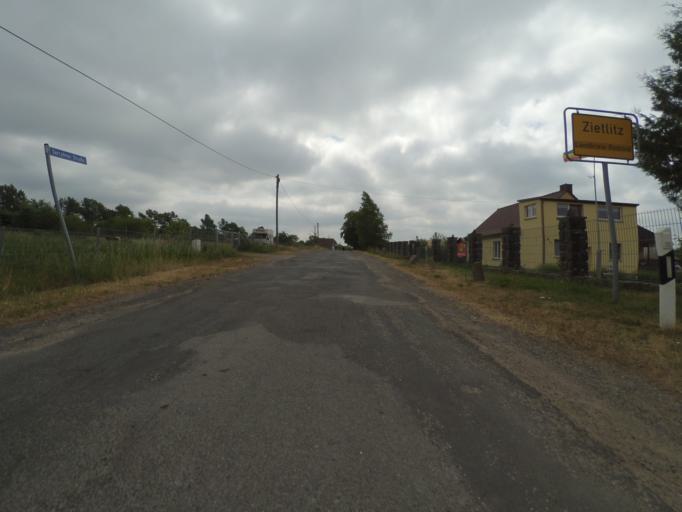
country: DE
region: Mecklenburg-Vorpommern
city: Krakow am See
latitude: 53.6349
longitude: 12.3450
